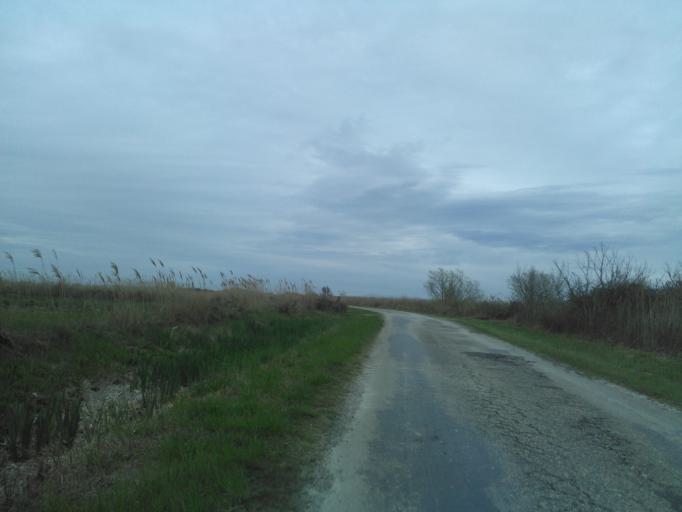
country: FR
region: Provence-Alpes-Cote d'Azur
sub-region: Departement des Bouches-du-Rhone
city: Arles
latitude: 43.5912
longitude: 4.5422
